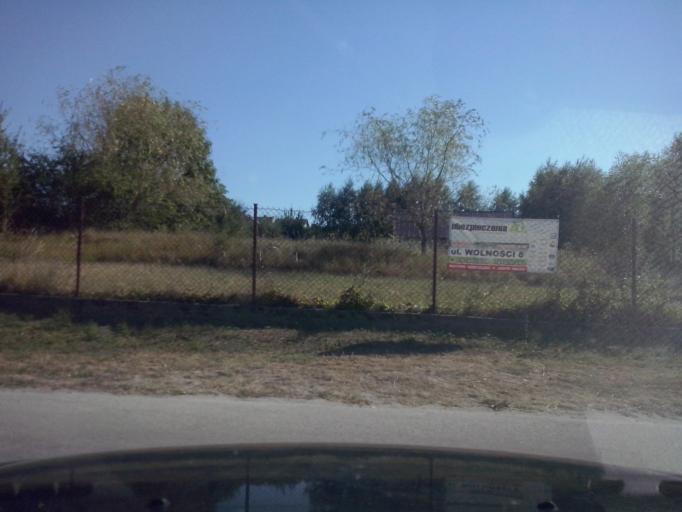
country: PL
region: Swietokrzyskie
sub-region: Powiat kielecki
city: Chmielnik
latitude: 50.6122
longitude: 20.7499
